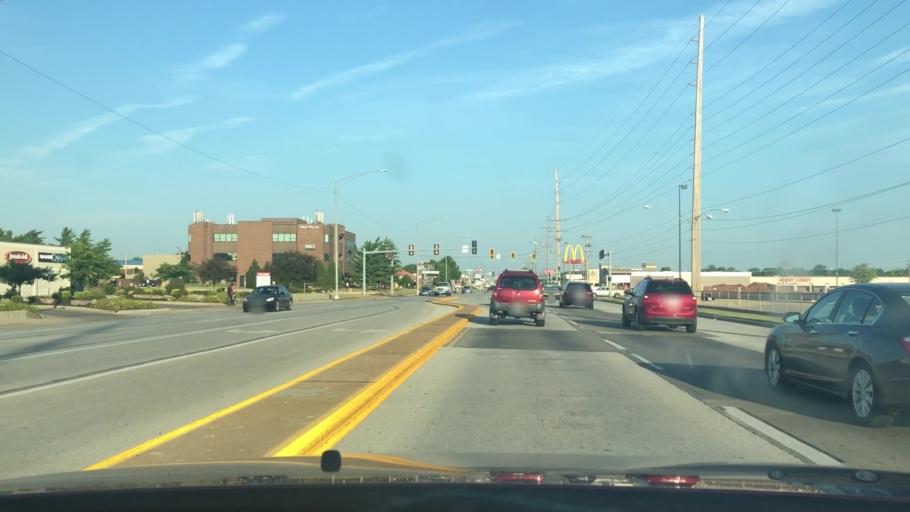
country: US
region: Missouri
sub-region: Greene County
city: Springfield
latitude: 37.1594
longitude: -93.2640
